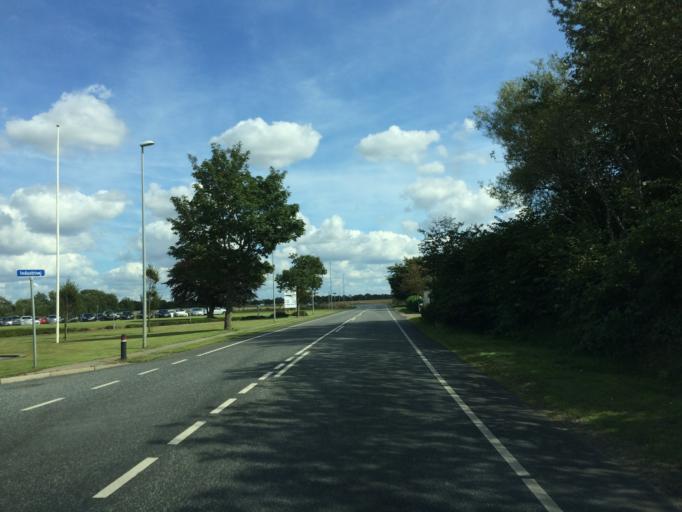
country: DK
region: Central Jutland
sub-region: Ringkobing-Skjern Kommune
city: Skjern
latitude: 56.0261
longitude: 8.3977
